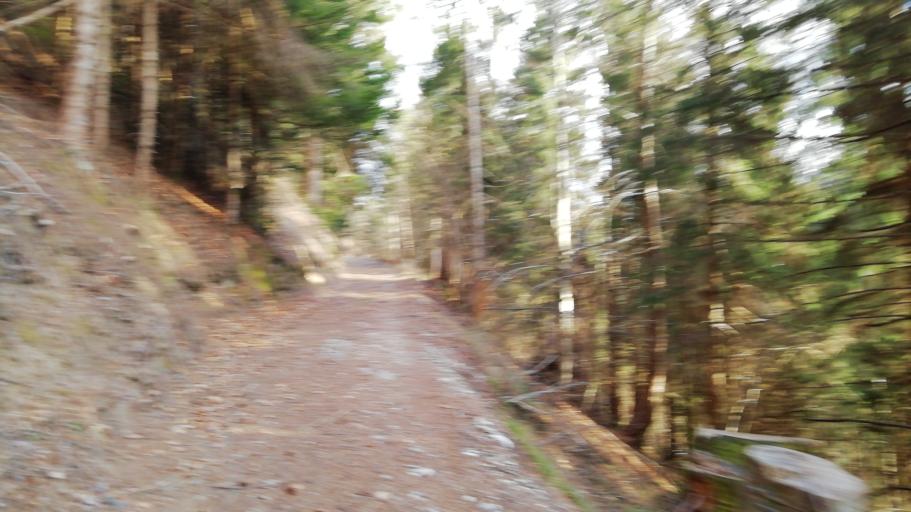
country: IT
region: Veneto
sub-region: Provincia di Belluno
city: Valle di Cadore
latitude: 46.4240
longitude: 12.3110
